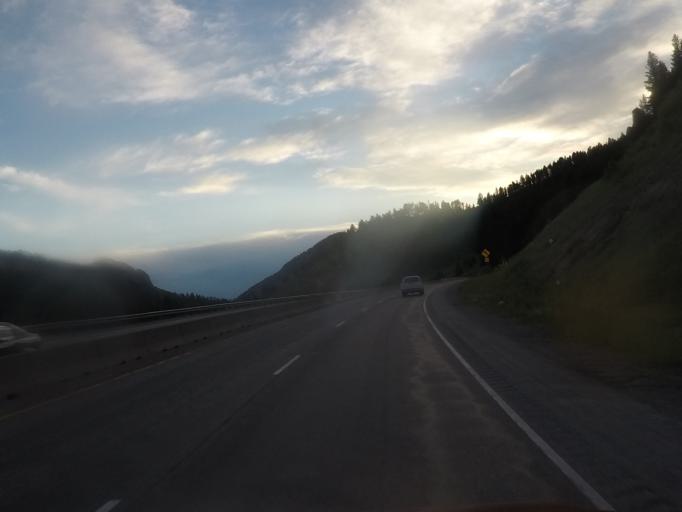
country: US
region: Montana
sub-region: Gallatin County
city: Bozeman
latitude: 45.6482
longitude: -110.8663
